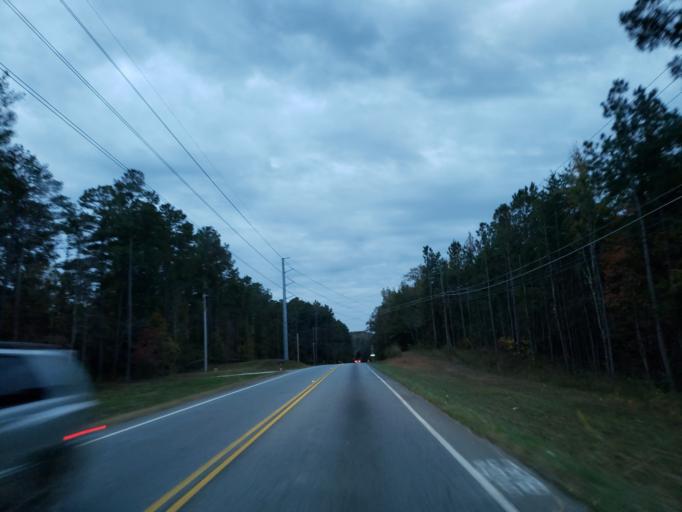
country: US
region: Georgia
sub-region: Paulding County
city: Hiram
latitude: 33.9609
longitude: -84.7395
